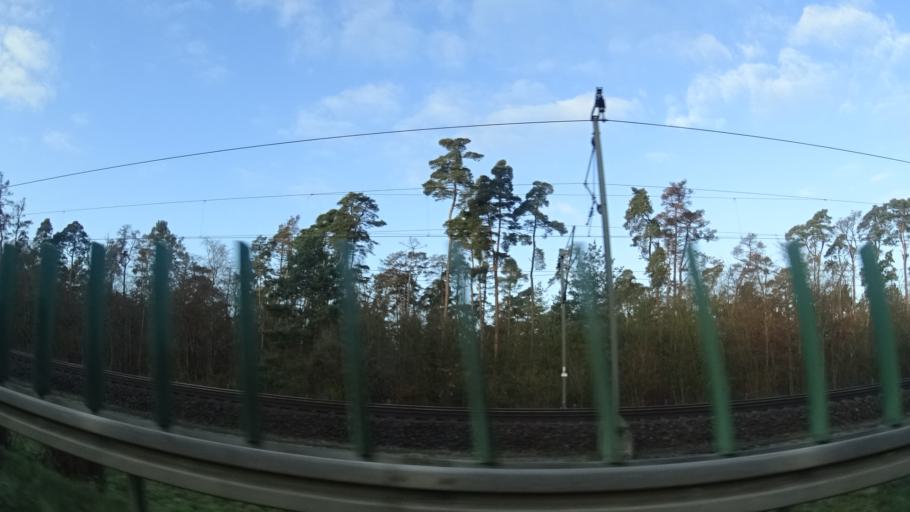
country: DE
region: Baden-Wuerttemberg
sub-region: Karlsruhe Region
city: Waghausel
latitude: 49.2382
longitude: 8.4963
